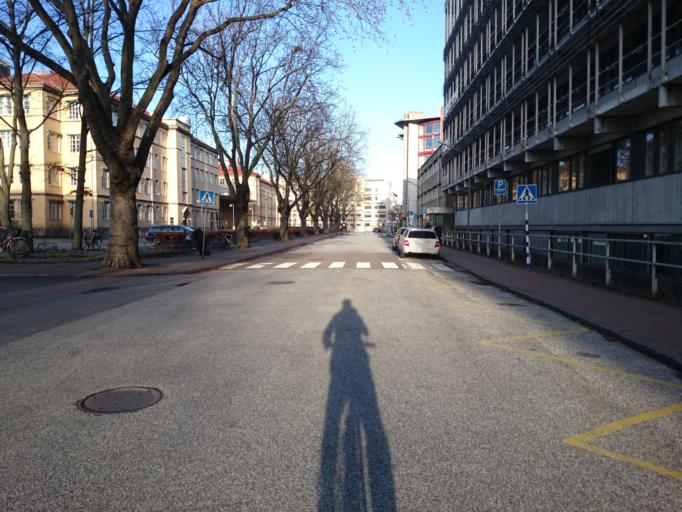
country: SE
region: Skane
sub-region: Malmo
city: Malmoe
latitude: 55.5878
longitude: 13.0007
